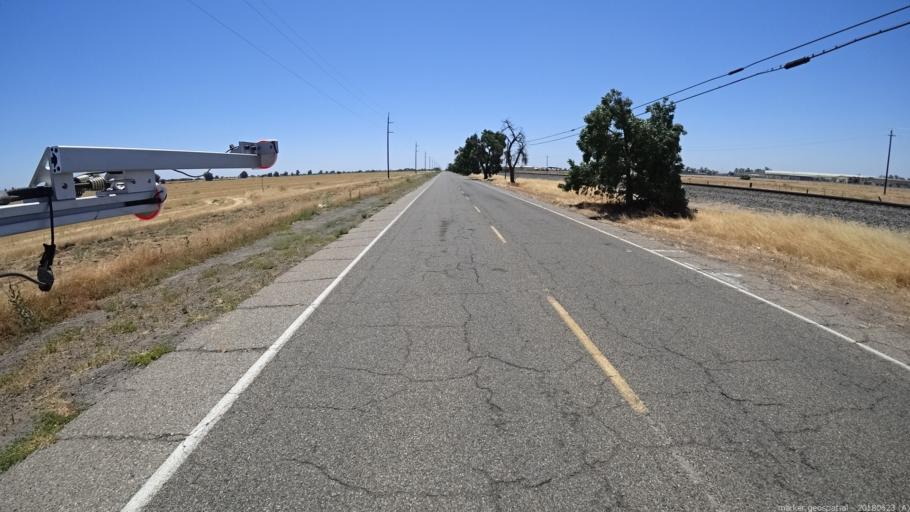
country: US
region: California
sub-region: Madera County
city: Chowchilla
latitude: 37.1151
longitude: -120.2448
